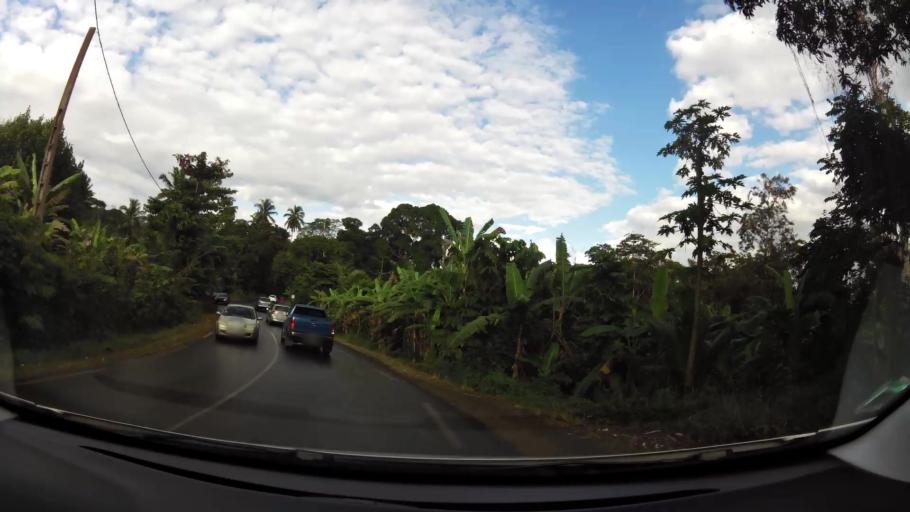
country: YT
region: Ouangani
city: Ouangani
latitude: -12.8358
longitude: 45.1452
